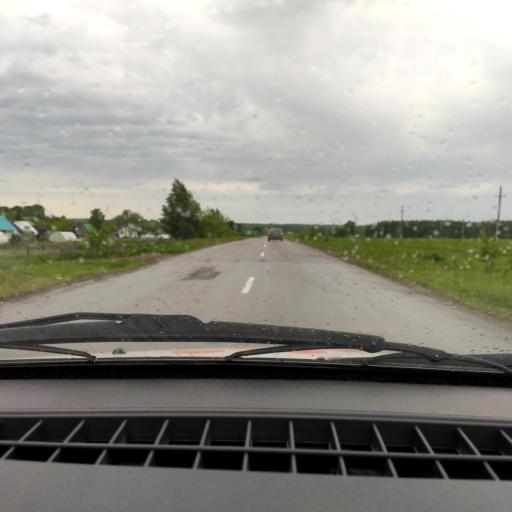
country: RU
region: Bashkortostan
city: Kudeyevskiy
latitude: 54.8463
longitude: 56.7957
